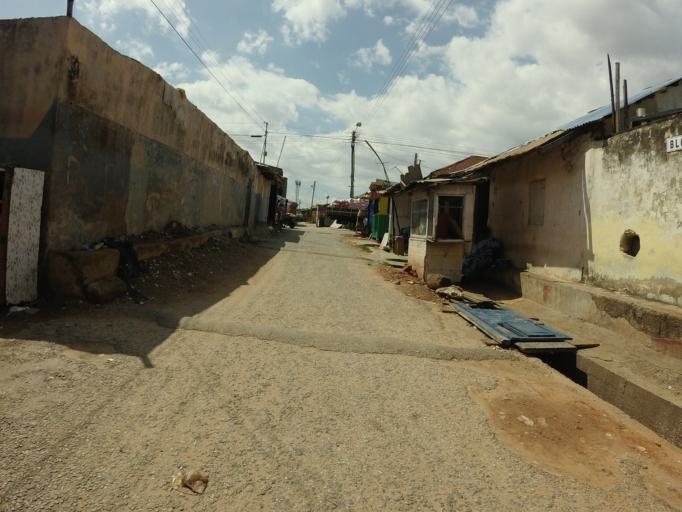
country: GH
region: Greater Accra
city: Accra
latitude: 5.5826
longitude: -0.1965
